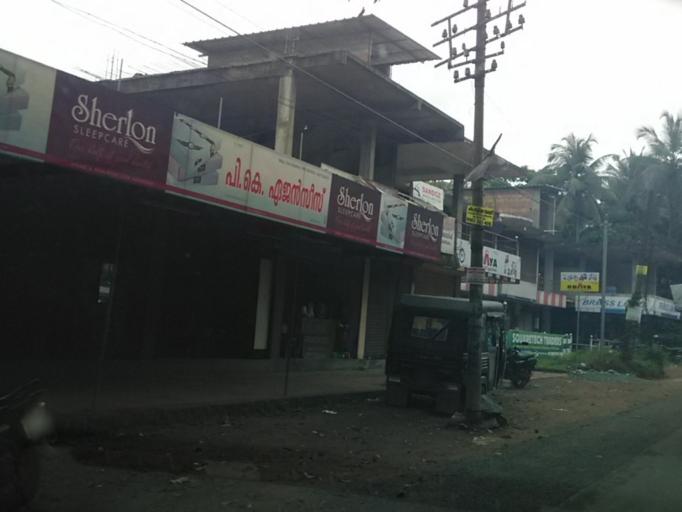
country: IN
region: Kerala
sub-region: Kozhikode
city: Kunnamangalam
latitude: 11.3072
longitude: 75.8812
